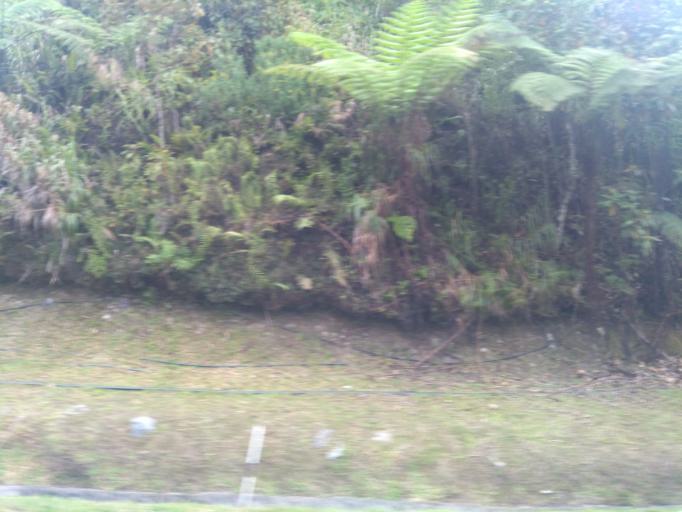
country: MY
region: Pahang
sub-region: Cameron Highlands
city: Tanah Rata
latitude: 4.5232
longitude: 101.4292
